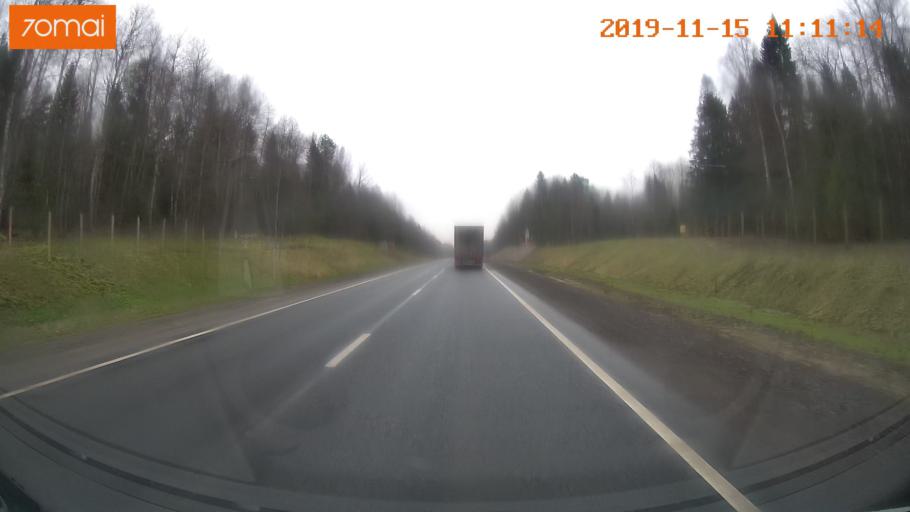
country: RU
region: Vologda
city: Chebsara
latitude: 59.1213
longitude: 39.1390
